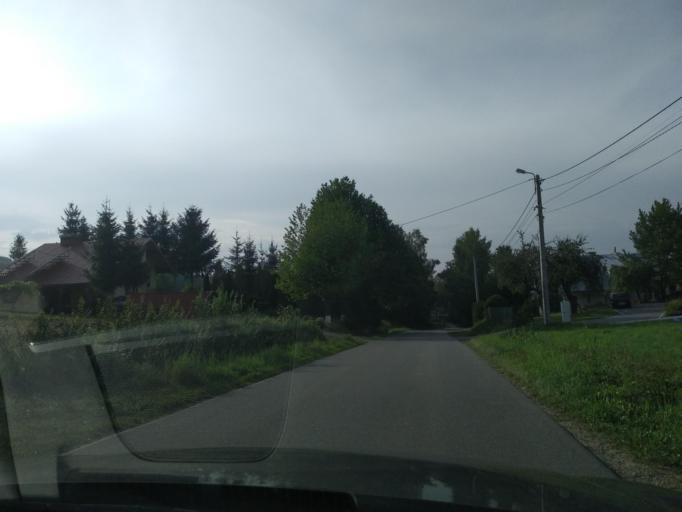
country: PL
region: Subcarpathian Voivodeship
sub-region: Powiat brzozowski
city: Dydnia
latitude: 49.6551
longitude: 22.2030
